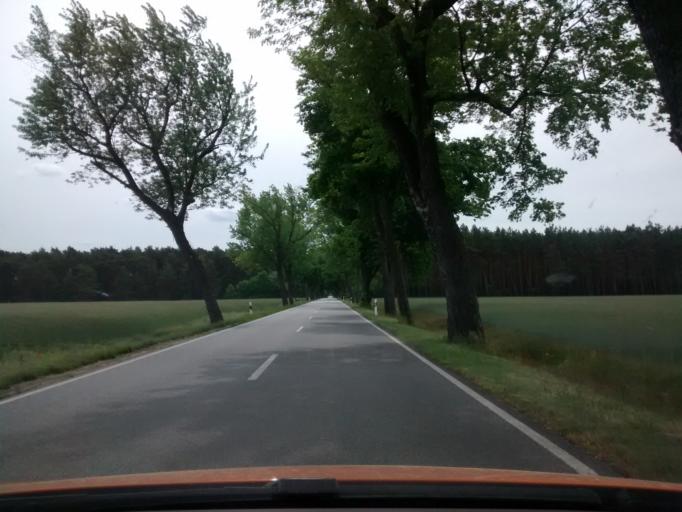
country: DE
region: Saxony-Anhalt
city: Holzdorf
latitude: 51.8907
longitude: 13.1415
